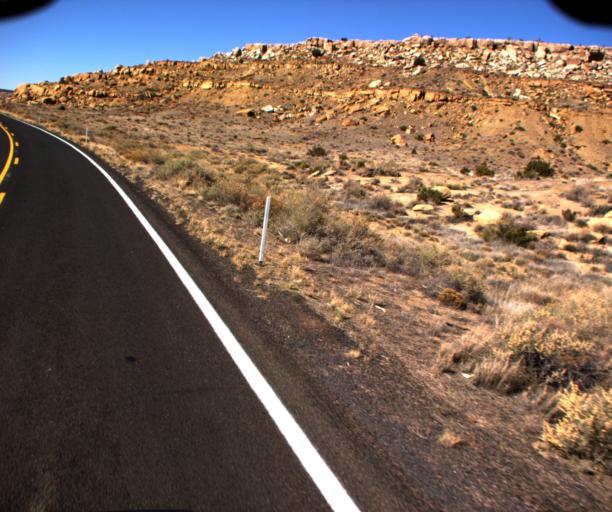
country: US
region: Arizona
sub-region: Navajo County
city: First Mesa
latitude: 35.8929
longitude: -110.6545
